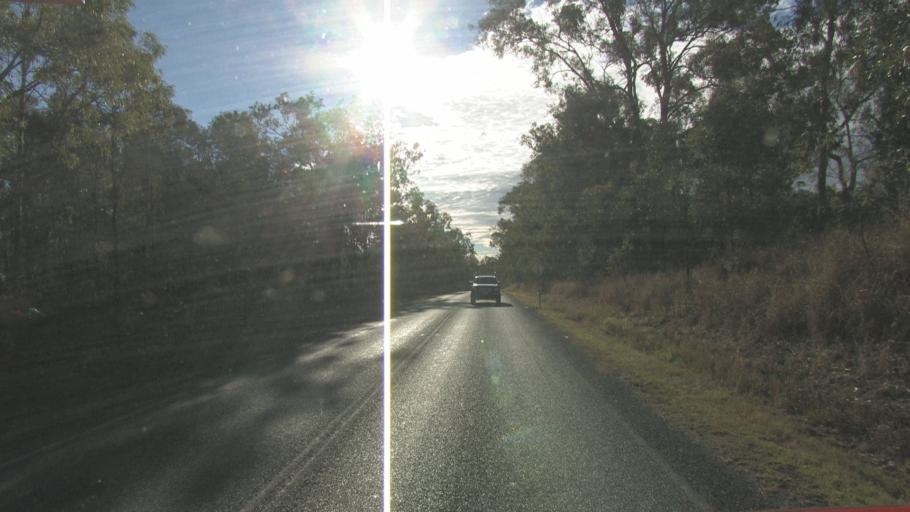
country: AU
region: Queensland
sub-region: Logan
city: Cedar Vale
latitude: -27.8898
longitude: 153.0832
